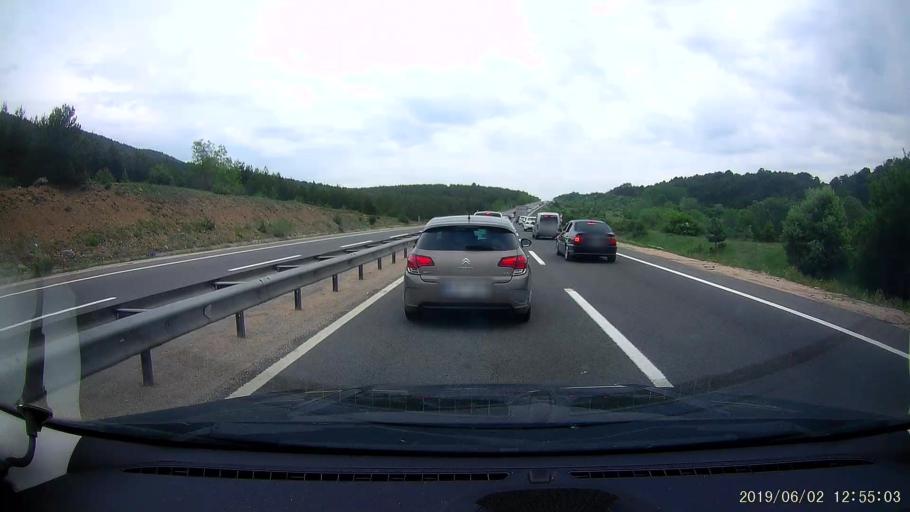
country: TR
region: Bolu
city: Gerede
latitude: 40.8289
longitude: 32.3667
